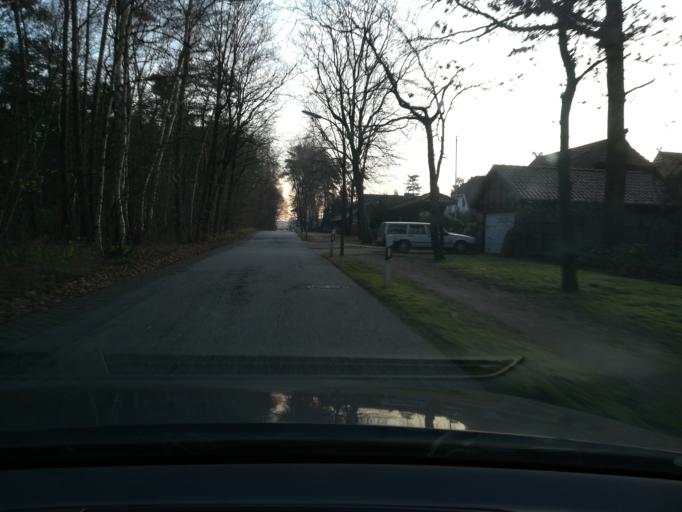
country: DE
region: Schleswig-Holstein
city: Escheburg
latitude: 53.4462
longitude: 10.3108
